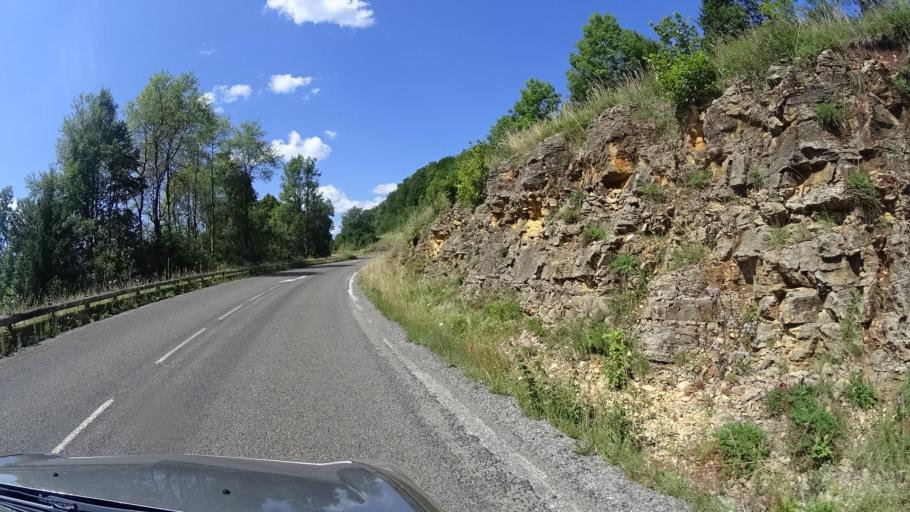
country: FR
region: Franche-Comte
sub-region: Departement du Jura
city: Longchaumois
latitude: 46.5064
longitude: 5.9524
